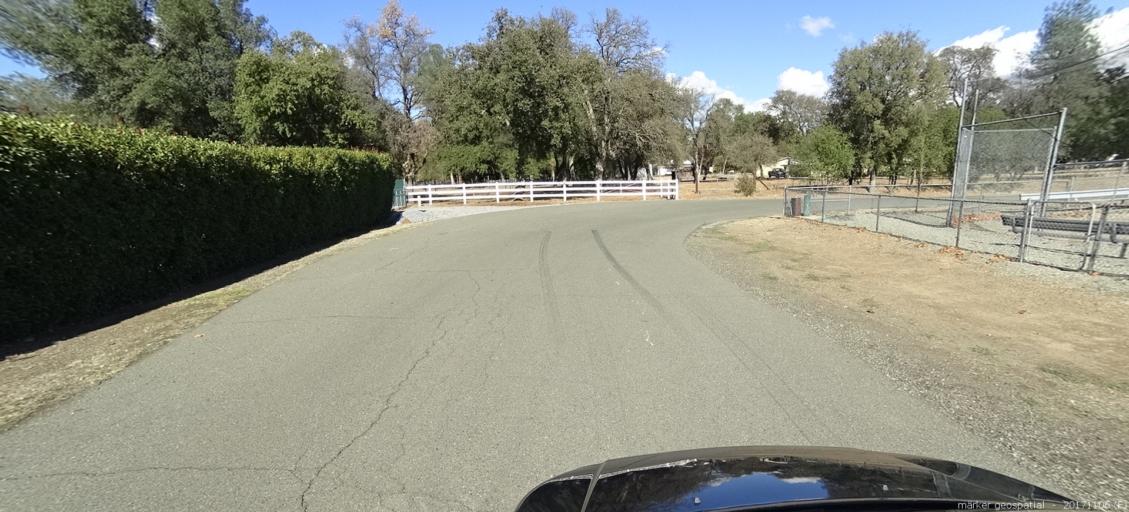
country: US
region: California
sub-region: Shasta County
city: Palo Cedro
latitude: 40.5944
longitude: -122.2312
